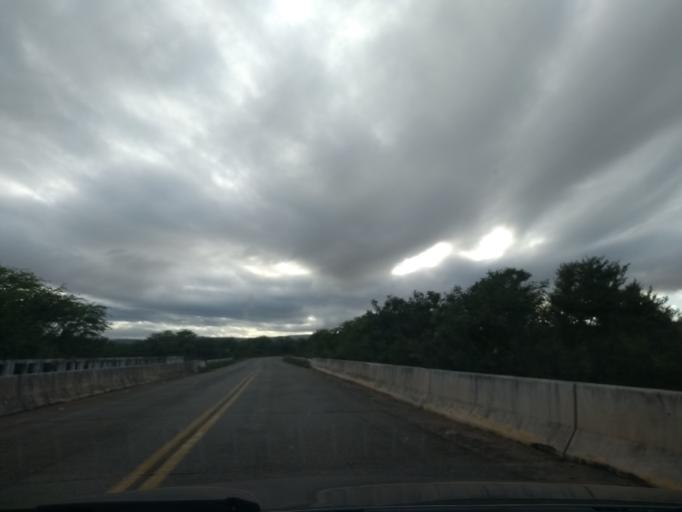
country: BR
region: Bahia
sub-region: Ituacu
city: Ituacu
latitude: -13.7678
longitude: -41.0425
